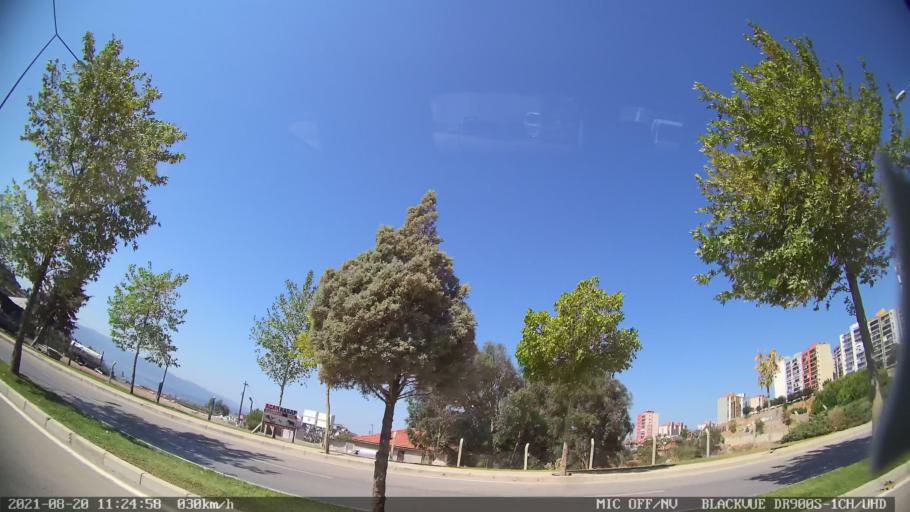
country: TR
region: Izmir
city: Karsiyaka
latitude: 38.5034
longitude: 27.0828
